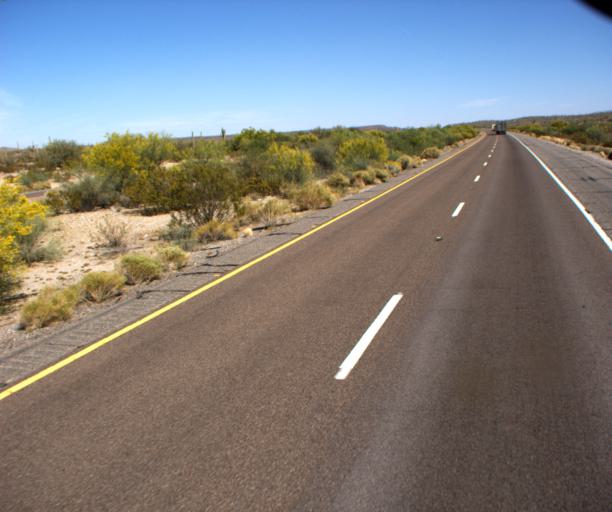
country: US
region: Arizona
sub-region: Maricopa County
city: Gila Bend
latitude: 32.8508
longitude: -112.3577
